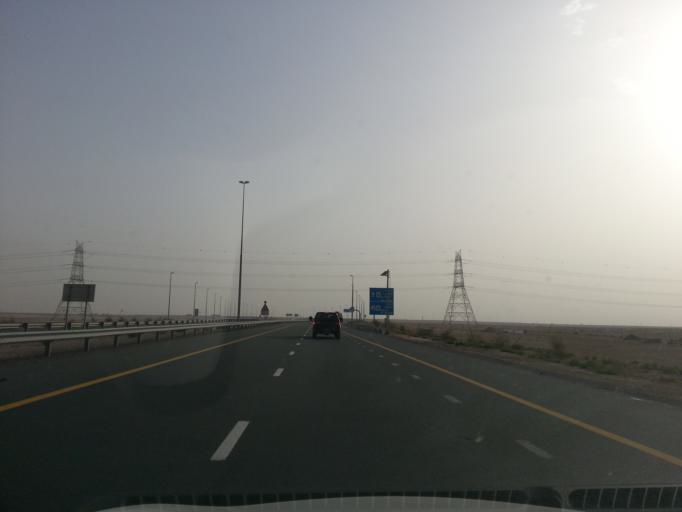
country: AE
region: Dubai
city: Dubai
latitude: 24.7994
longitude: 55.0871
